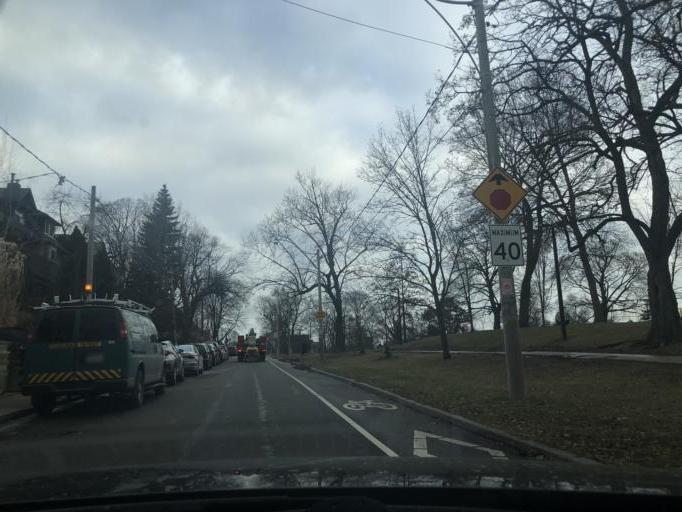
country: CA
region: Ontario
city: Toronto
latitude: 43.6741
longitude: -79.3481
